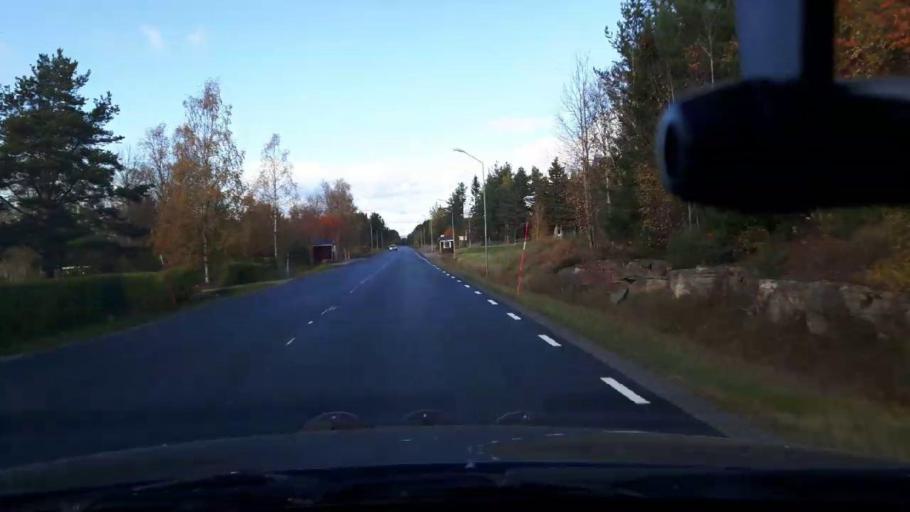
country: SE
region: Jaemtland
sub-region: Bergs Kommun
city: Hoverberg
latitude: 62.9692
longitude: 14.4876
